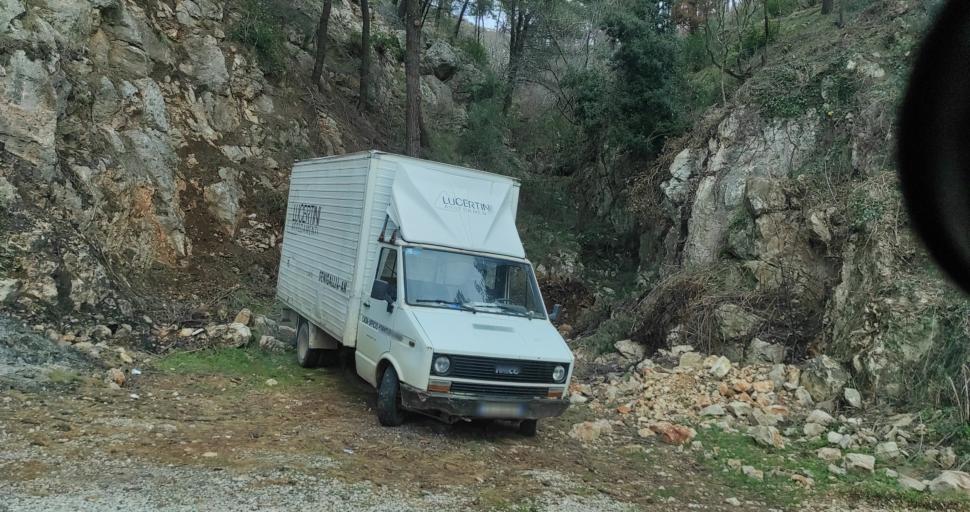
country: AL
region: Lezhe
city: Shengjin
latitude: 41.8175
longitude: 19.5676
